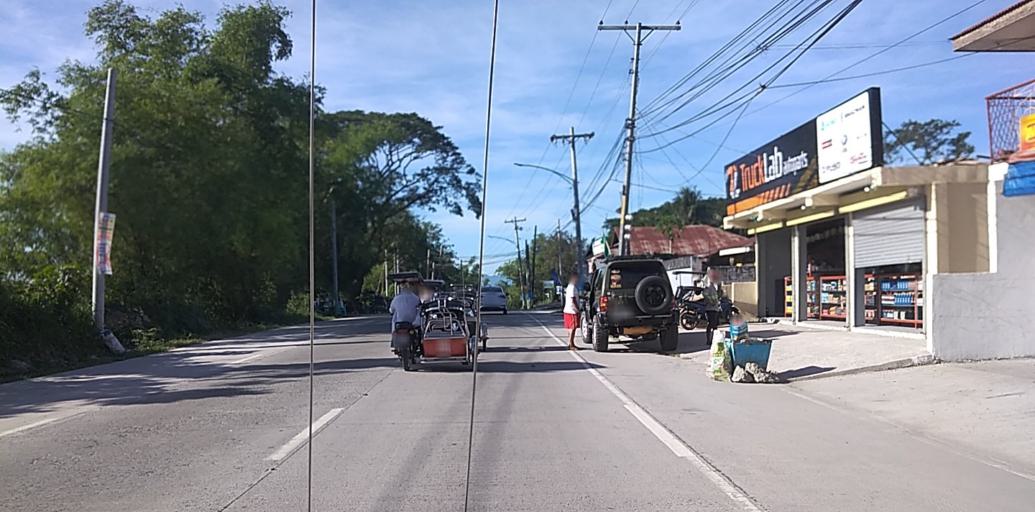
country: PH
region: Central Luzon
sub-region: Province of Pampanga
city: Porac
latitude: 15.0797
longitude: 120.5467
